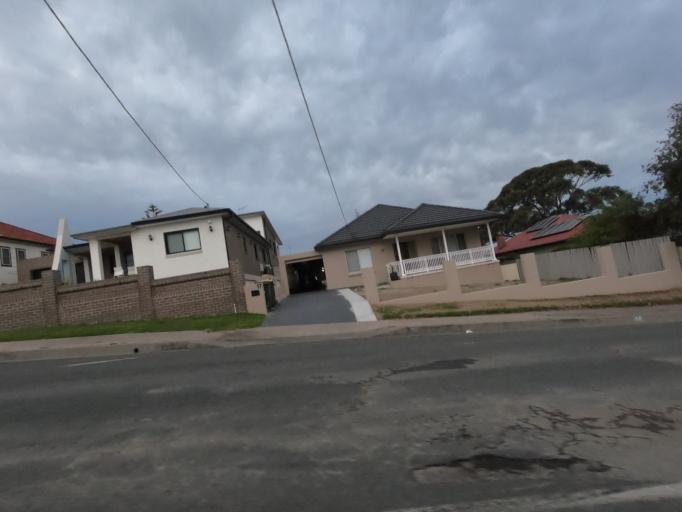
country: AU
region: New South Wales
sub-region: Wollongong
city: Lake Heights
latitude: -34.4806
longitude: 150.8682
